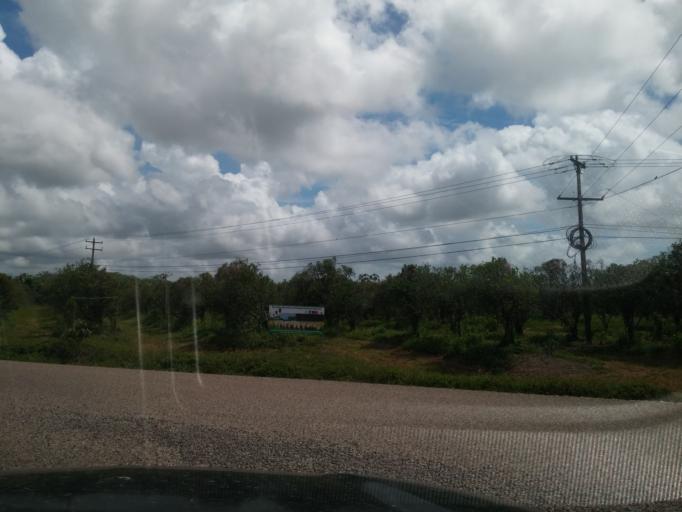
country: BZ
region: Stann Creek
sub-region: Dangriga
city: Dangriga
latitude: 16.9805
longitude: -88.2947
